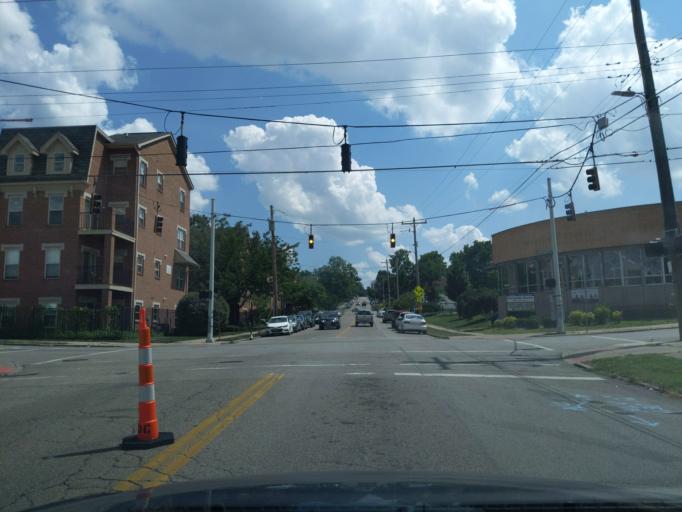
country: US
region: Ohio
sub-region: Hamilton County
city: Saint Bernard
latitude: 39.1329
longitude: -84.5059
